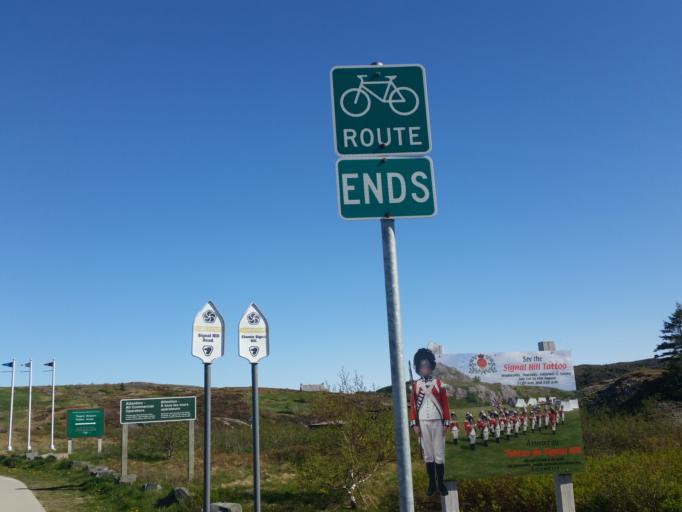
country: CA
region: Newfoundland and Labrador
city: St. John's
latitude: 47.5718
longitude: -52.6875
